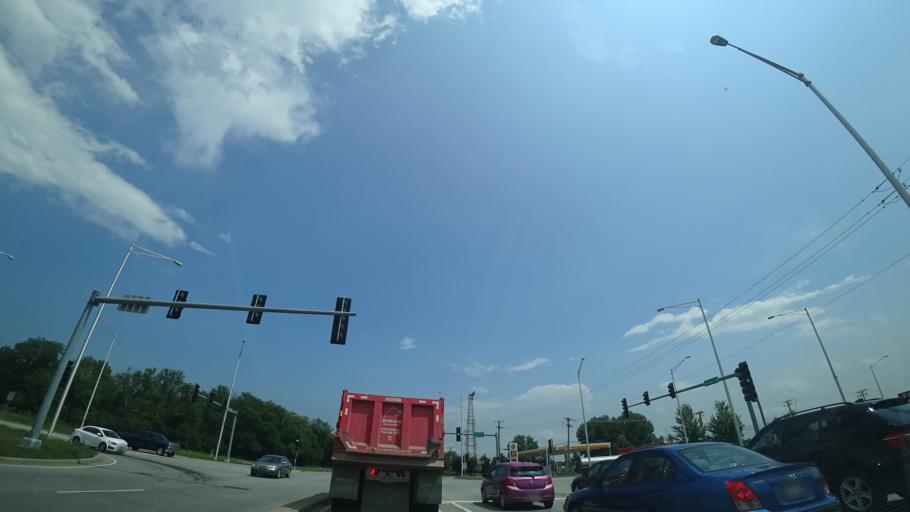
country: US
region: Illinois
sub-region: Cook County
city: Matteson
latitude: 41.5281
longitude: -87.7331
